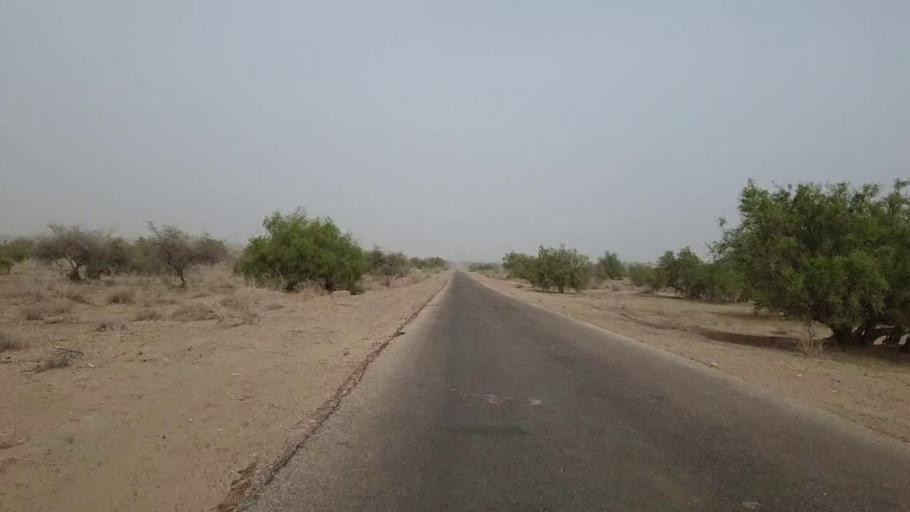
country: PK
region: Sindh
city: Islamkot
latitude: 24.5677
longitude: 70.3275
